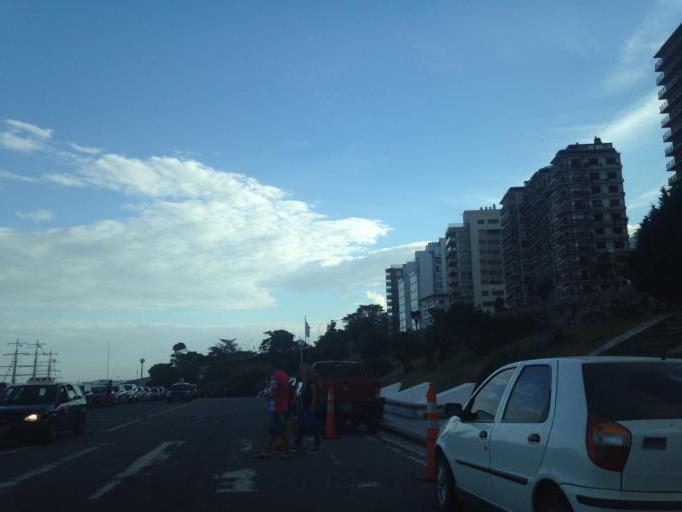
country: AR
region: Buenos Aires
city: Mar del Plata
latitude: -38.0280
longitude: -57.5332
